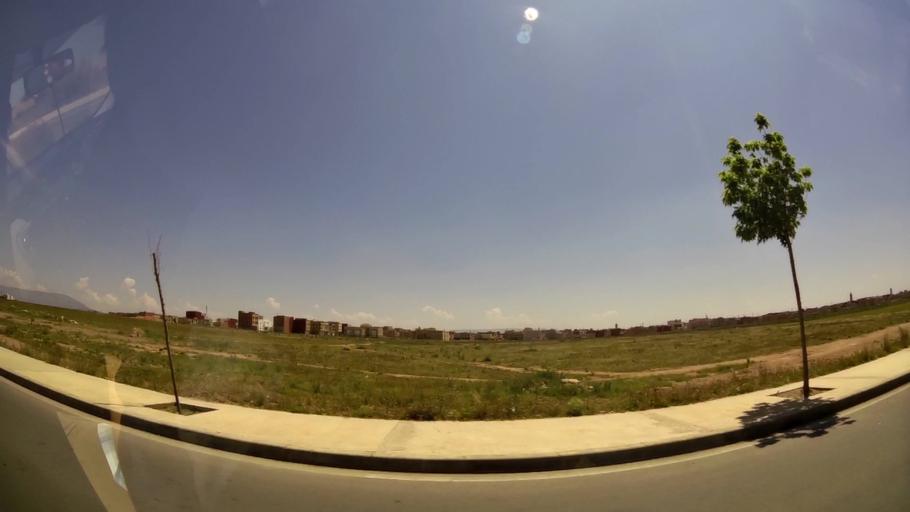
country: MA
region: Oriental
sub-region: Oujda-Angad
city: Oujda
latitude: 34.6952
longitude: -1.9307
